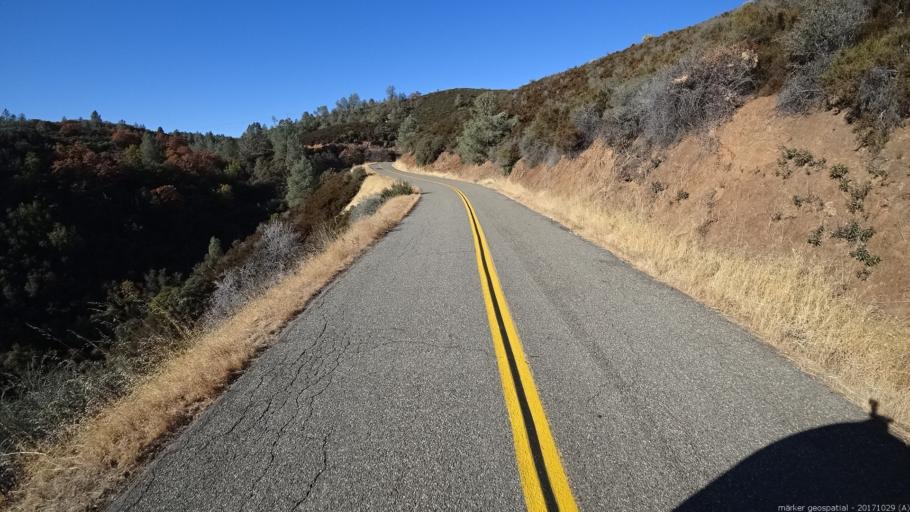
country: US
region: California
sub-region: Trinity County
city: Lewiston
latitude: 40.3675
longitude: -122.8768
